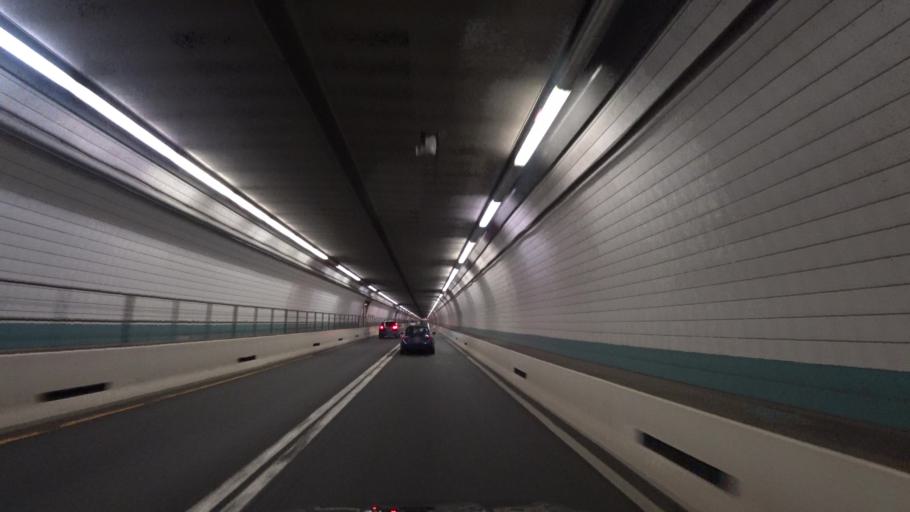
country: US
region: Massachusetts
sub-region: Suffolk County
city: South Boston
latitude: 42.3512
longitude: -71.0313
